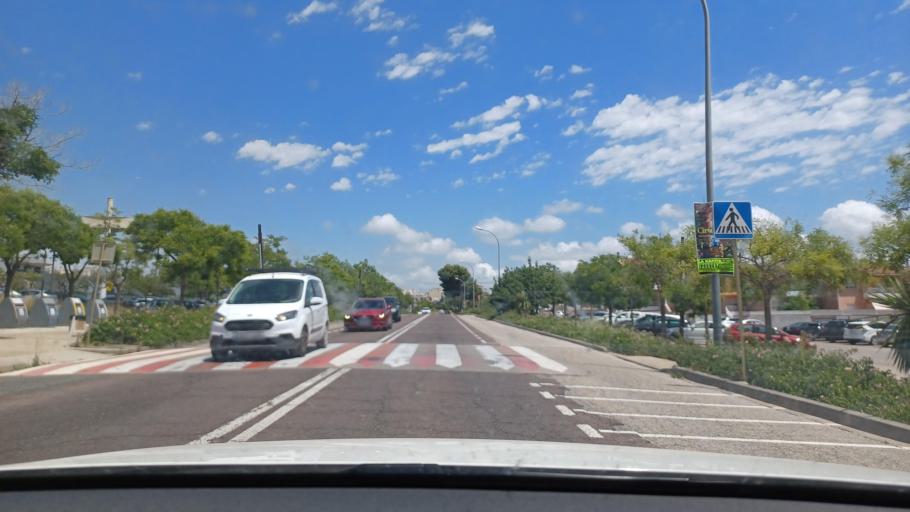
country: ES
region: Catalonia
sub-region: Provincia de Tarragona
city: Sant Carles de la Rapita
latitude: 40.6091
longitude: 0.5839
